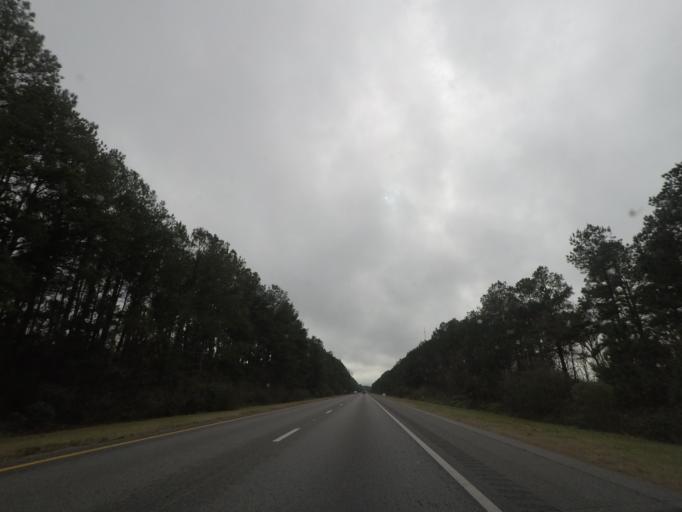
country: US
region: South Carolina
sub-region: Orangeburg County
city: Holly Hill
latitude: 33.3659
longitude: -80.5255
